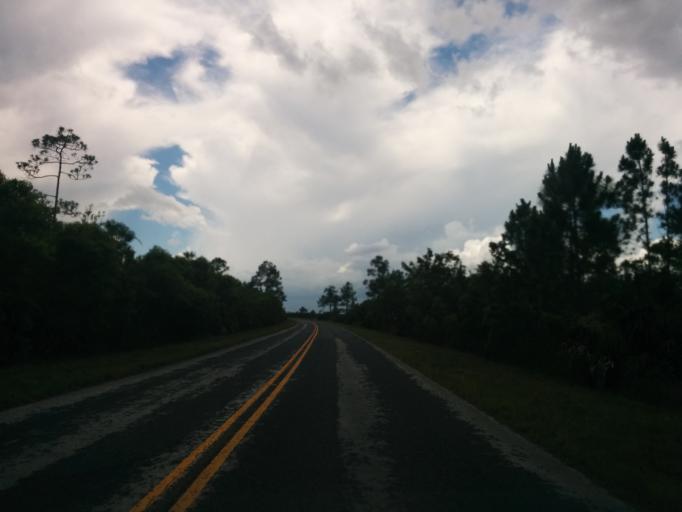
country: US
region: Florida
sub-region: Miami-Dade County
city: Florida City
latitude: 25.4358
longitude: -80.6979
